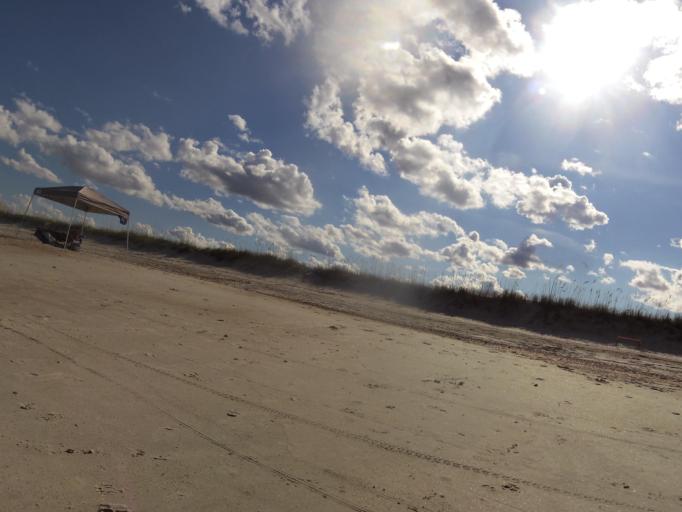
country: US
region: Florida
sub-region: Nassau County
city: Fernandina Beach
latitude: 30.6963
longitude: -81.4272
